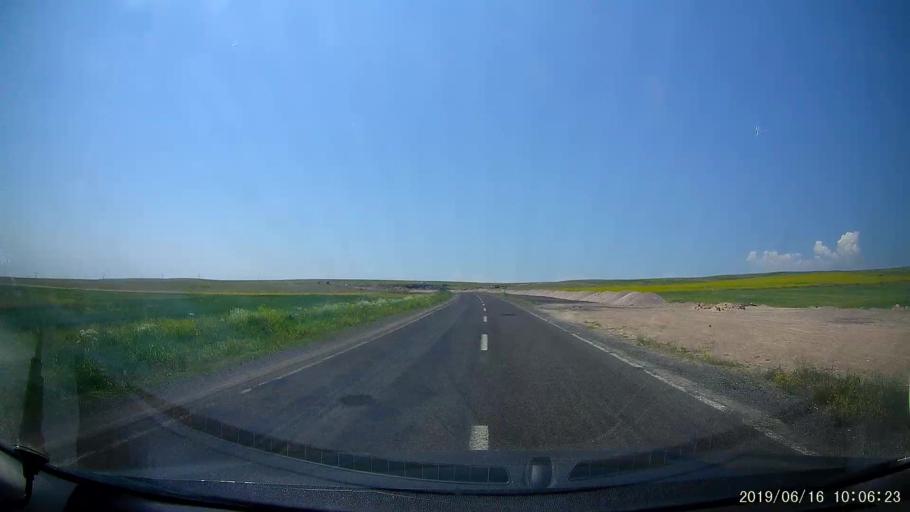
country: TR
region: Kars
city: Digor
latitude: 40.2559
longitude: 43.5421
